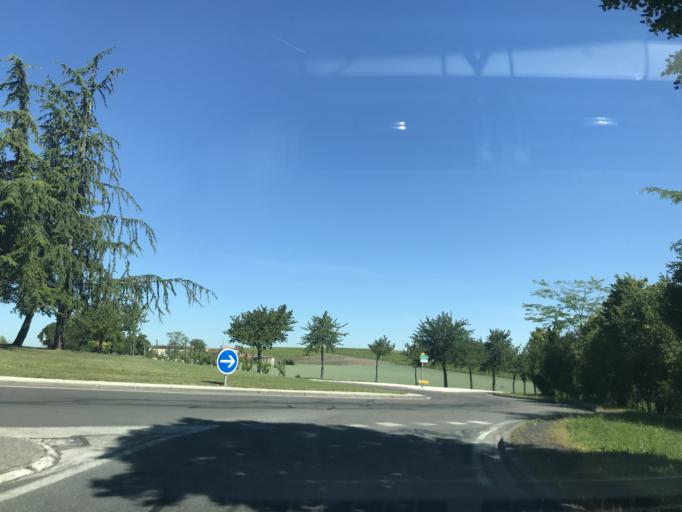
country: FR
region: Poitou-Charentes
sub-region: Departement de la Charente
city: Segonzac
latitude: 45.5284
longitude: -0.3048
